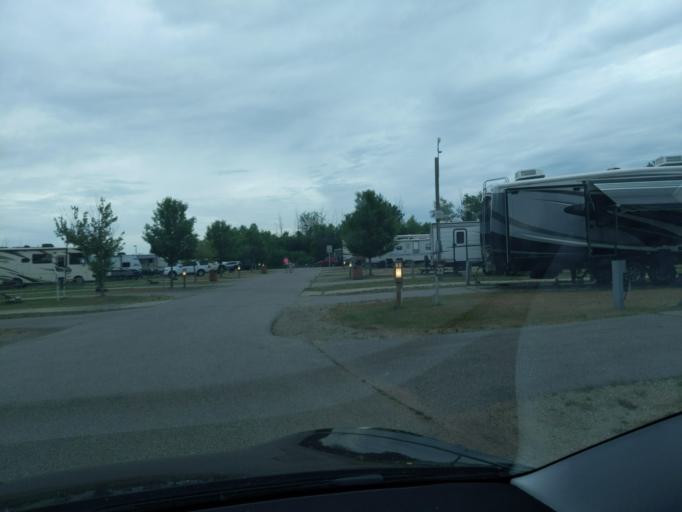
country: US
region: Michigan
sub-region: Isabella County
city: Mount Pleasant
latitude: 43.6174
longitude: -84.7387
